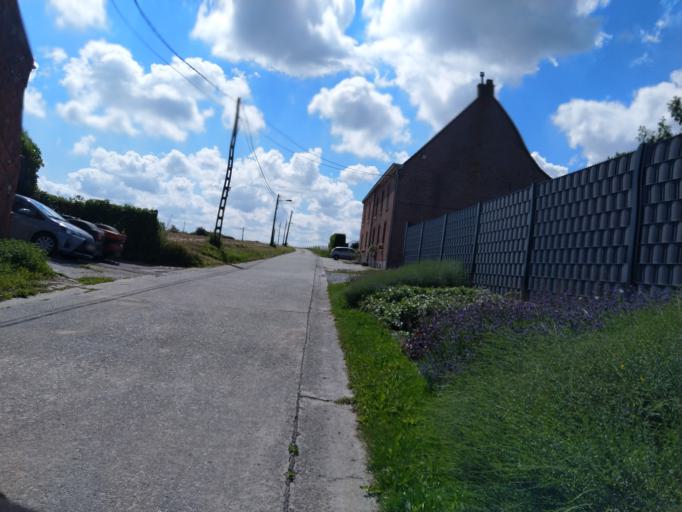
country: BE
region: Wallonia
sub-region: Province du Hainaut
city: Beloeil
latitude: 50.5709
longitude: 3.6835
